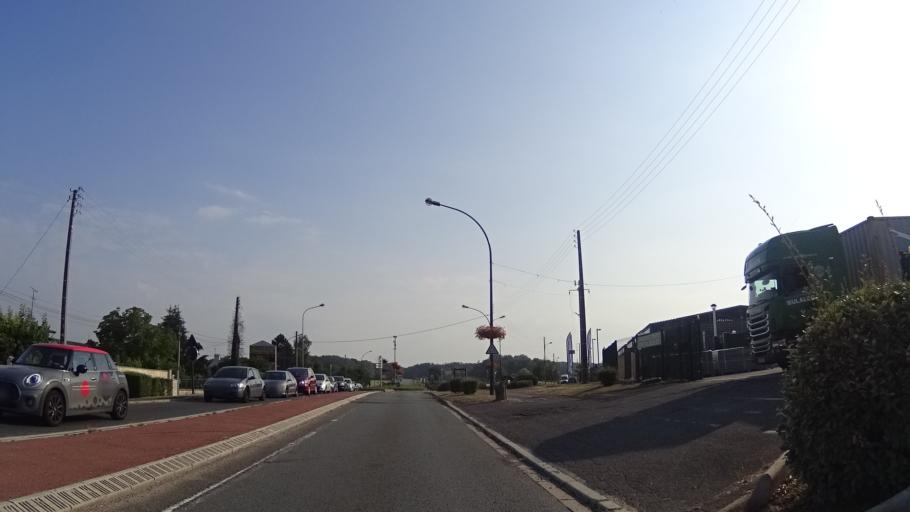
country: FR
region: Ile-de-France
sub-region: Departement du Val-d'Oise
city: Chaumontel
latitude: 49.1262
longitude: 2.4293
